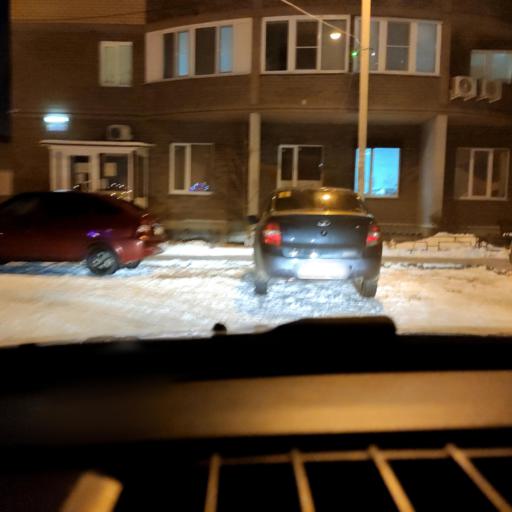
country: RU
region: Voronezj
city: Shilovo
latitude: 51.5683
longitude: 39.1242
